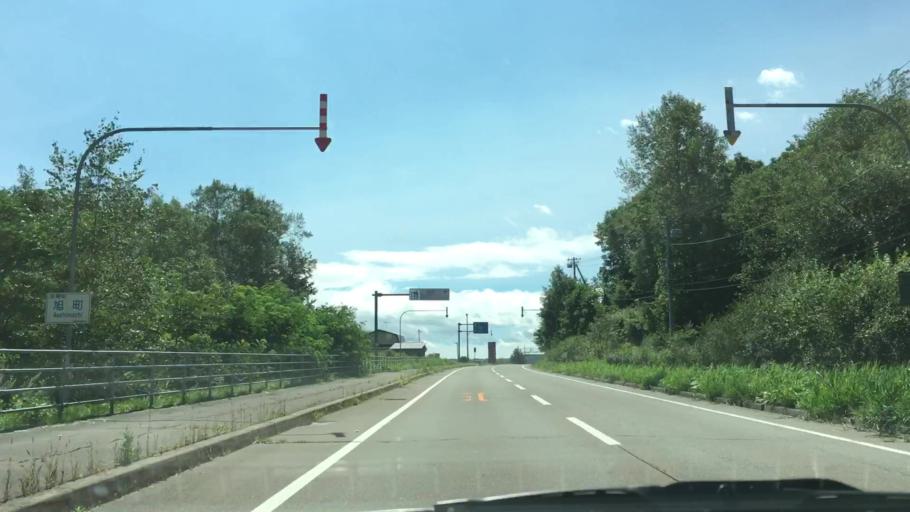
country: JP
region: Hokkaido
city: Otofuke
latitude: 43.2523
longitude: 143.5654
